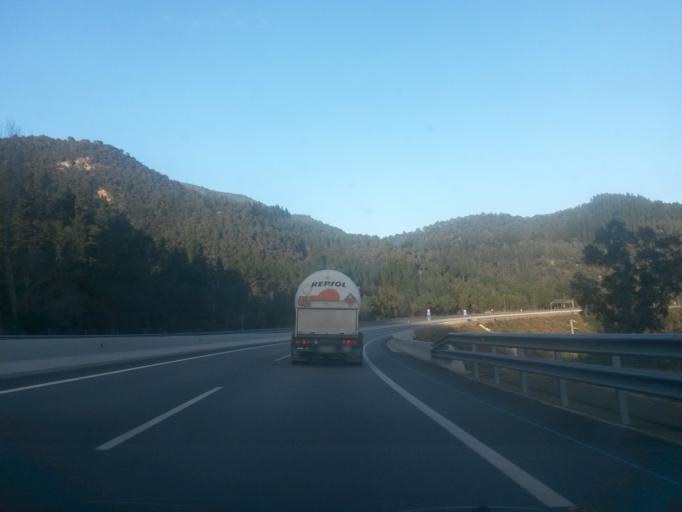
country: ES
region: Catalonia
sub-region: Provincia de Girona
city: Santa Coloma de Farners
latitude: 41.8708
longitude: 2.5938
